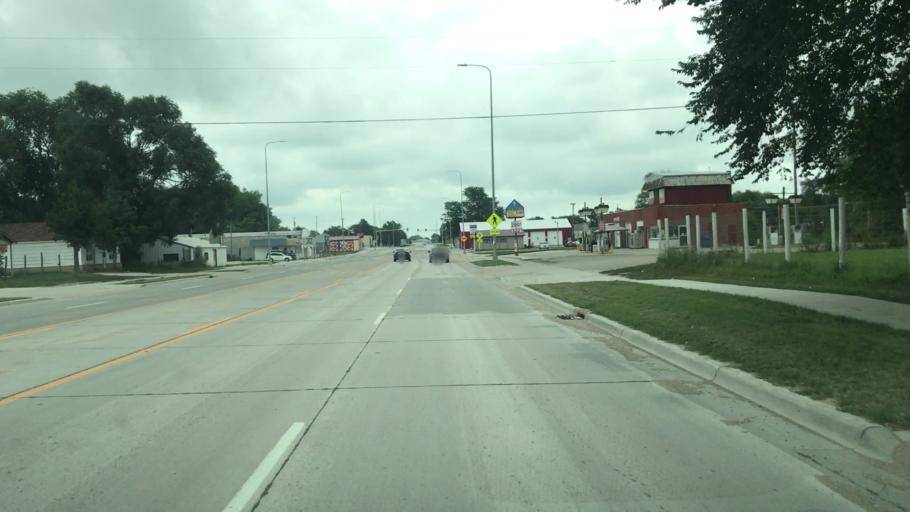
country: US
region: South Dakota
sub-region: Todd County
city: Mission
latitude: 43.3057
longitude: -100.6629
